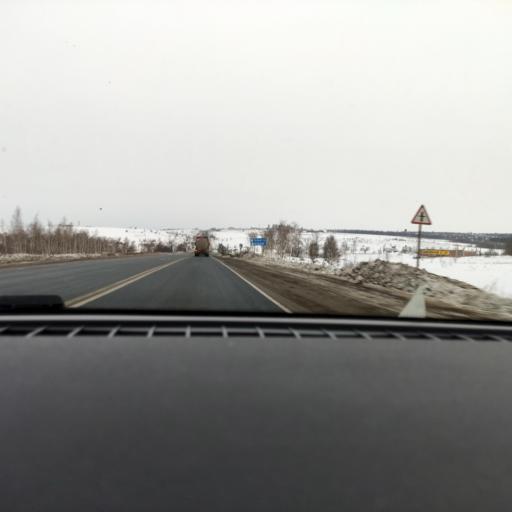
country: RU
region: Samara
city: Novosemeykino
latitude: 53.3735
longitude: 50.4335
